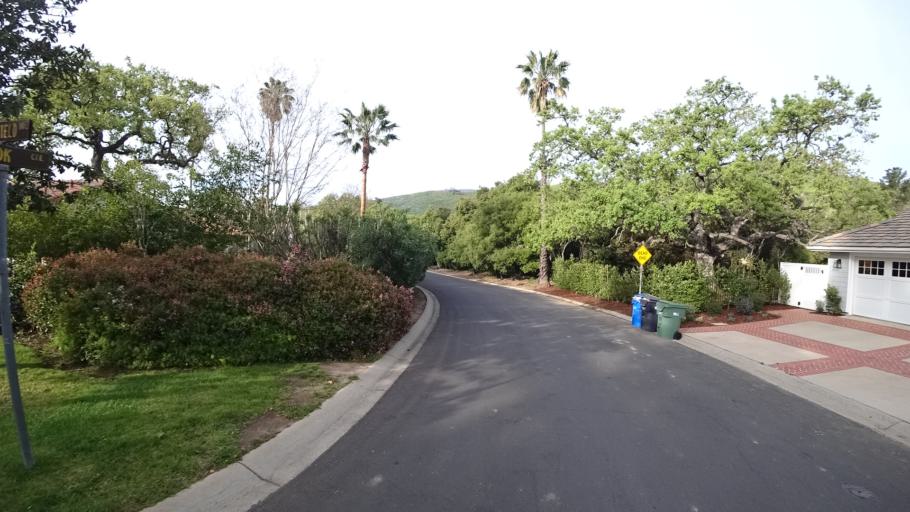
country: US
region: California
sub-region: Ventura County
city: Thousand Oaks
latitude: 34.1916
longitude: -118.8204
